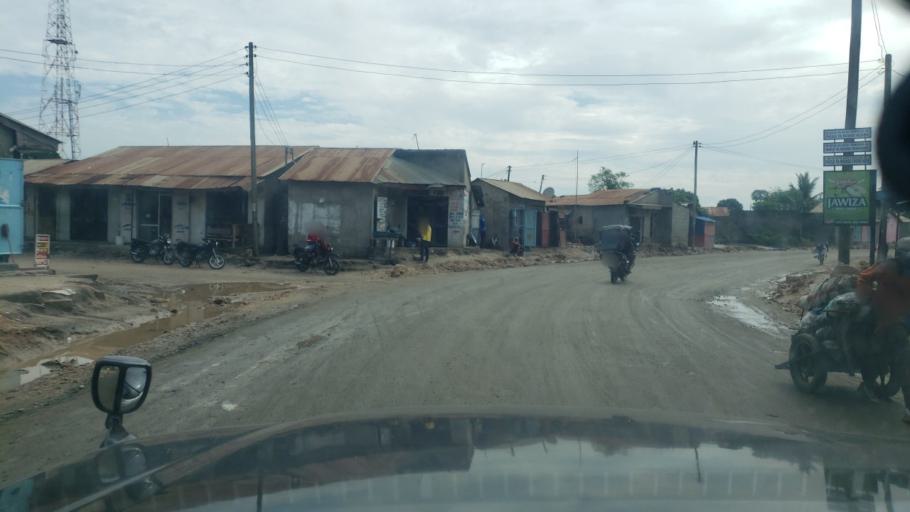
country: TZ
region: Pwani
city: Vikindu
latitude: -6.9272
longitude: 39.2546
